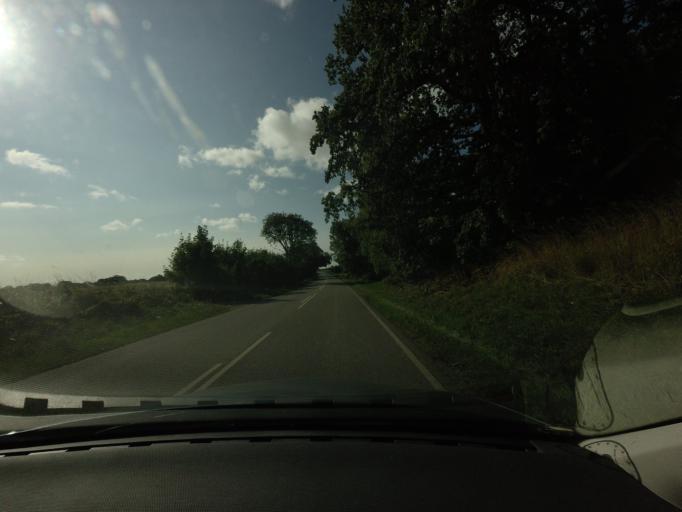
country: DK
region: Zealand
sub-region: Vordingborg Kommune
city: Praesto
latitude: 55.1323
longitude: 12.0195
